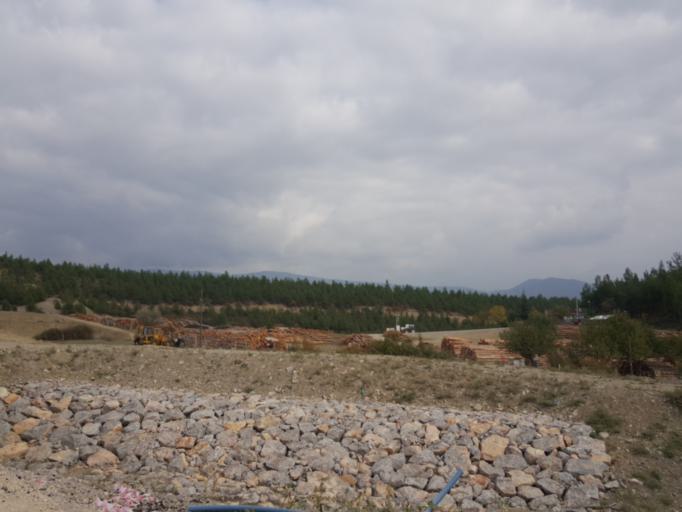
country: TR
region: Sinop
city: Duragan
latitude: 41.4312
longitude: 35.0531
